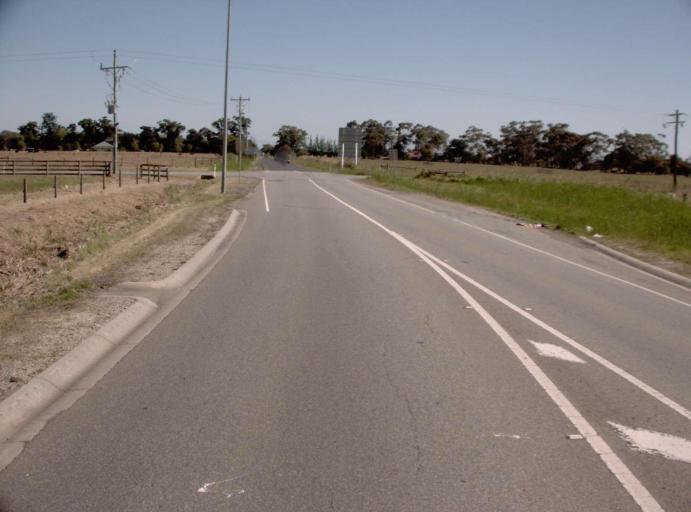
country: AU
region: Victoria
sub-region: Cardinia
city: Officer South
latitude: -38.0825
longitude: 145.4333
